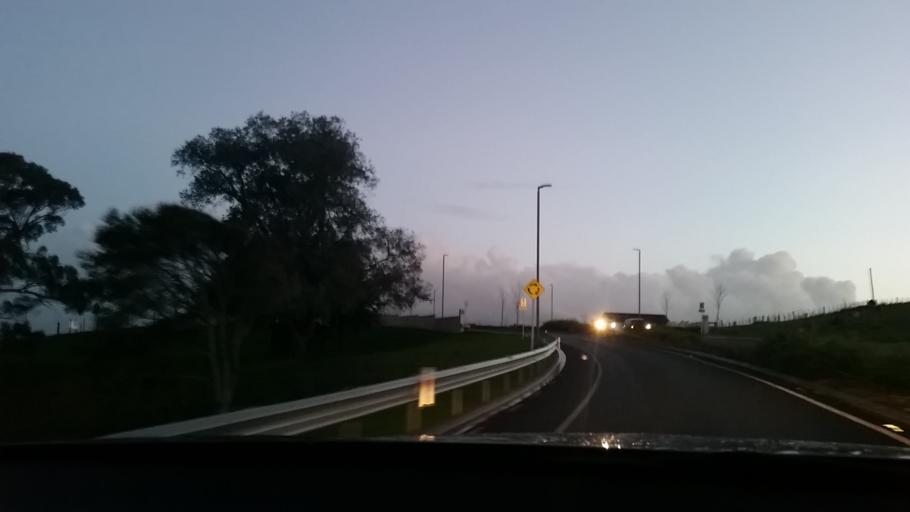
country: NZ
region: Waikato
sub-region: Hamilton City
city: Hamilton
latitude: -37.8173
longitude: 175.2271
